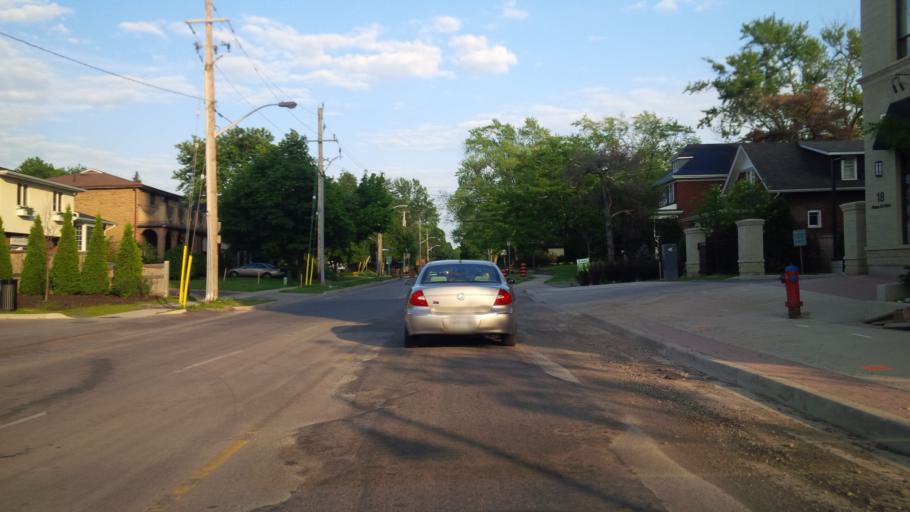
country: CA
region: Ontario
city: Hamilton
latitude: 43.3065
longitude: -79.8524
